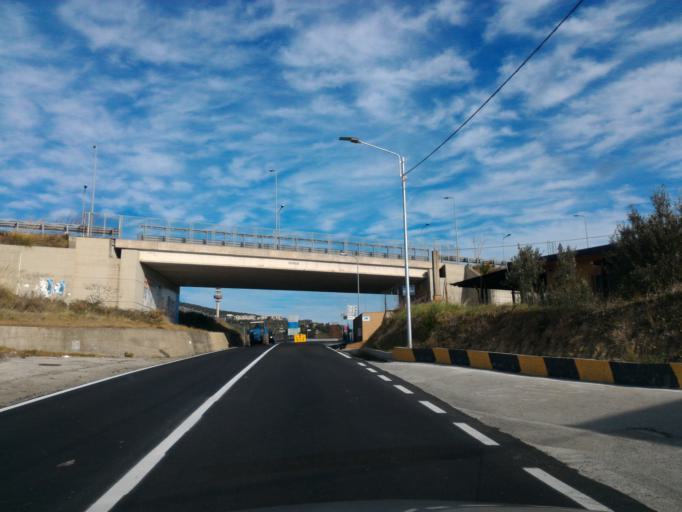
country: IT
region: Calabria
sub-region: Provincia di Catanzaro
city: Siano
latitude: 38.9113
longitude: 16.6017
